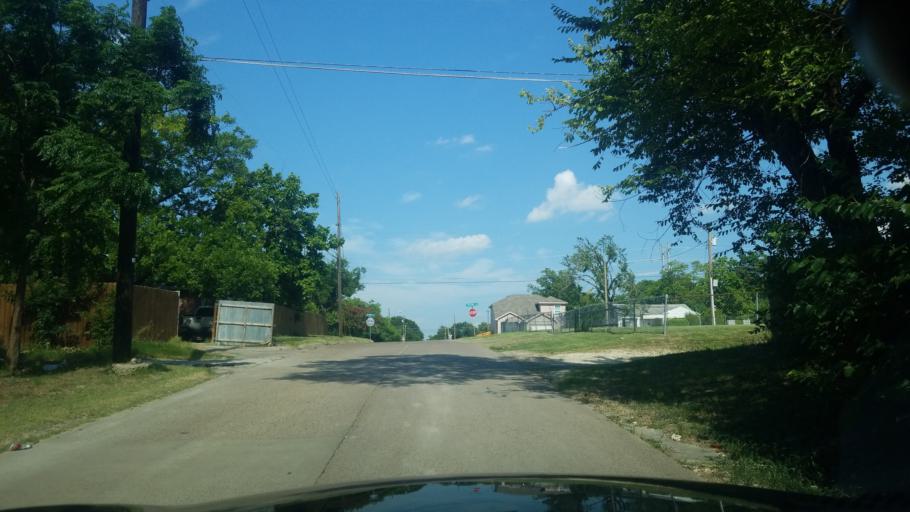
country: US
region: Texas
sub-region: Dallas County
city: Dallas
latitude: 32.7295
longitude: -96.8063
